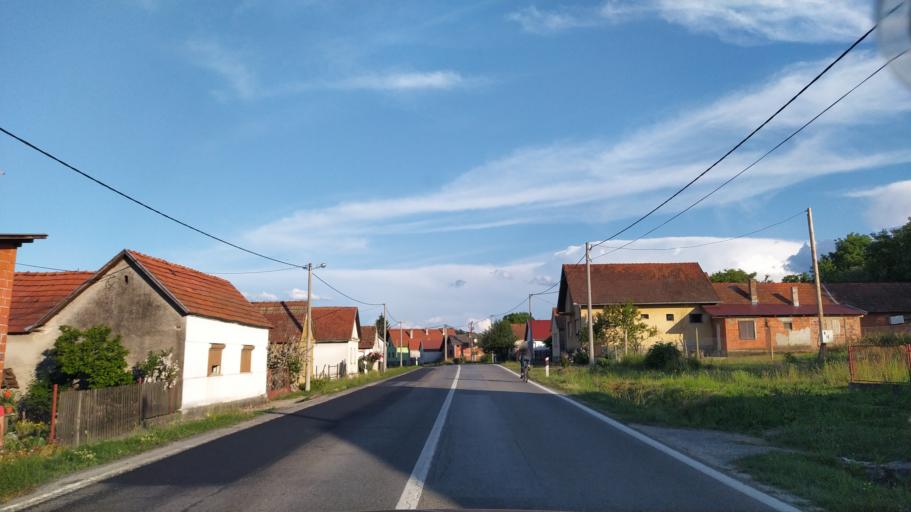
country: HR
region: Virovitick-Podravska
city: Slatina
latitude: 45.6792
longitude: 17.7457
